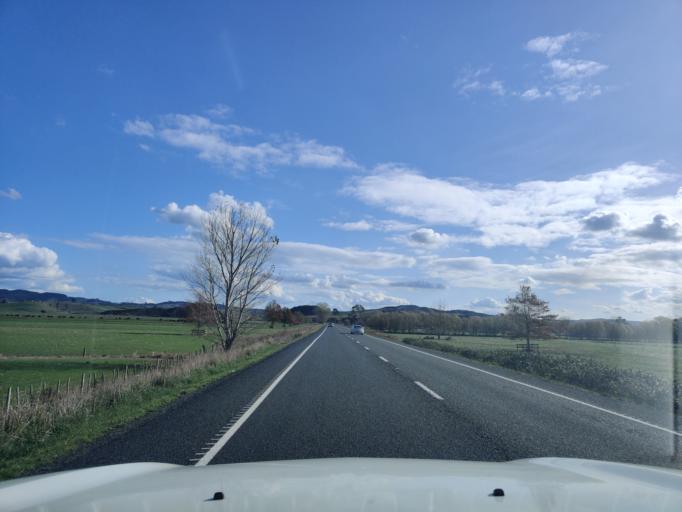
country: NZ
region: Waikato
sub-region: Hauraki District
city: Ngatea
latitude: -37.2808
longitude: 175.4179
